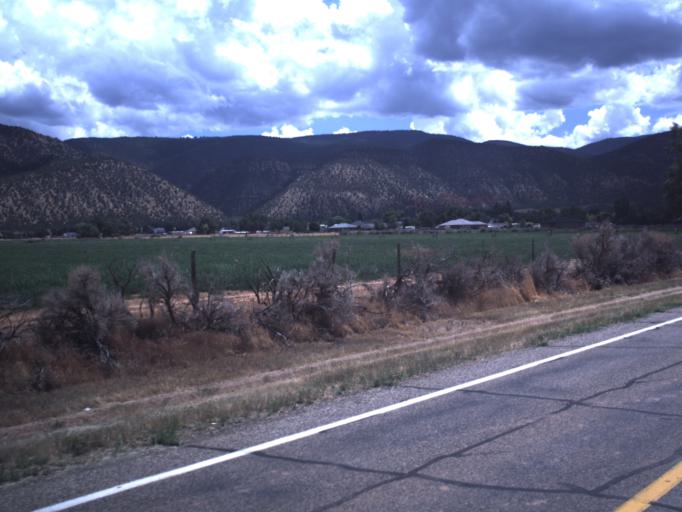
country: US
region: Utah
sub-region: Iron County
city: Parowan
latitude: 37.8955
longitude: -112.7749
